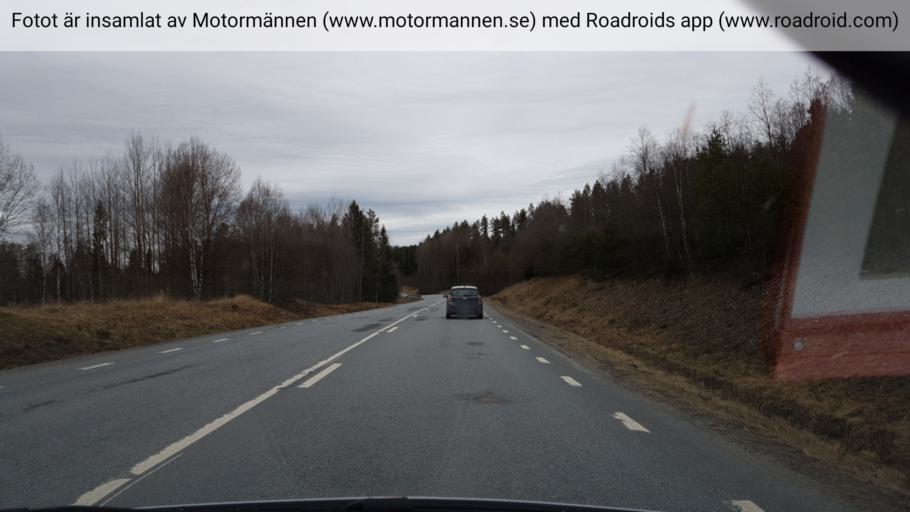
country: SE
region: Vaesternorrland
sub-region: Solleftea Kommun
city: Solleftea
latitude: 63.1986
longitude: 17.2345
